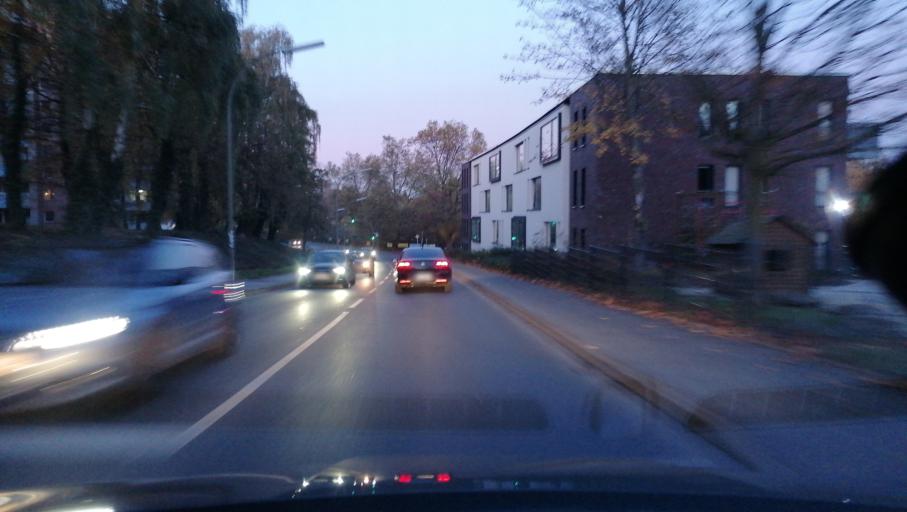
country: DE
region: North Rhine-Westphalia
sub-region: Regierungsbezirk Arnsberg
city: Dortmund
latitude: 51.4829
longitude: 7.5061
